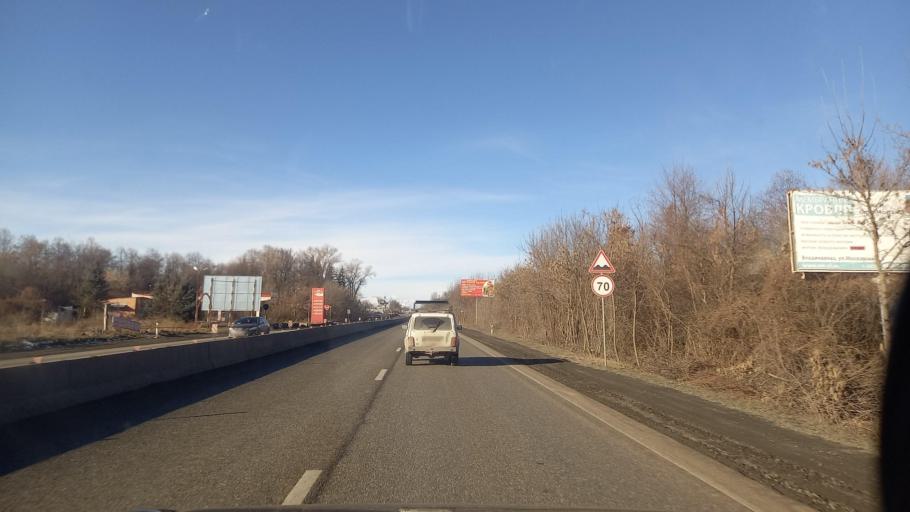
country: RU
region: North Ossetia
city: Gizel'
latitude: 43.0286
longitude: 44.5910
